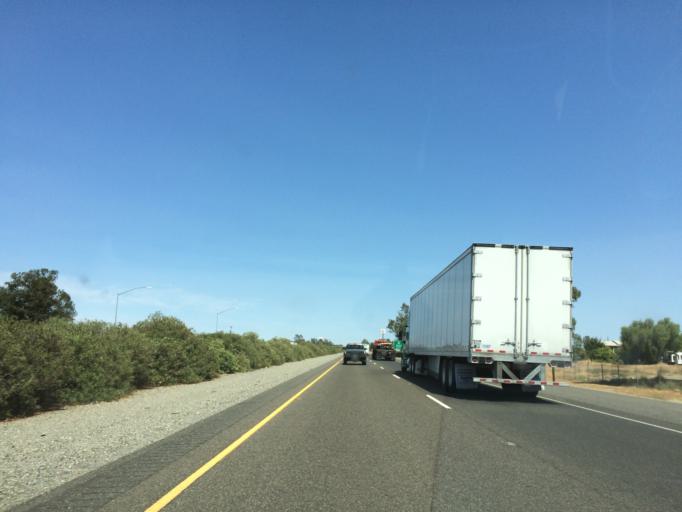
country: US
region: California
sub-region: Glenn County
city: Orland
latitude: 39.7415
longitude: -122.2056
